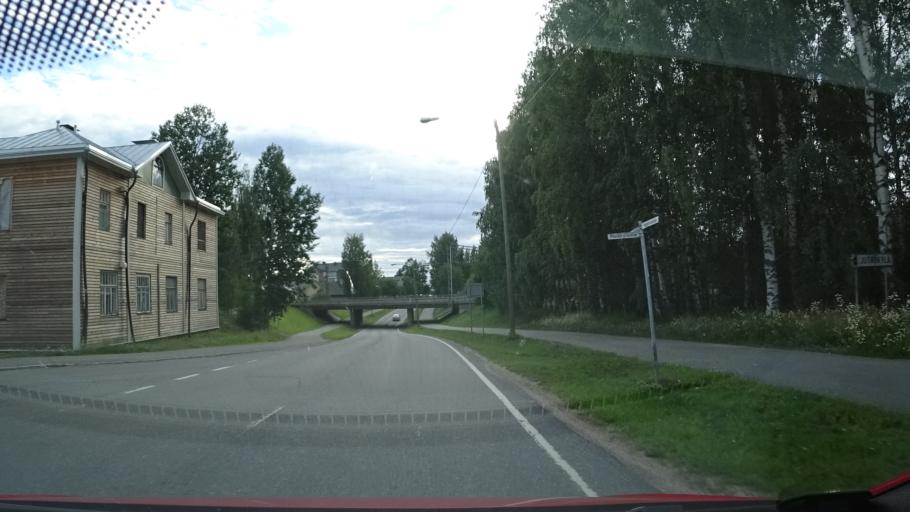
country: FI
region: Northern Ostrobothnia
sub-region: Oulu
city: Liminka
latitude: 64.8085
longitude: 25.4227
